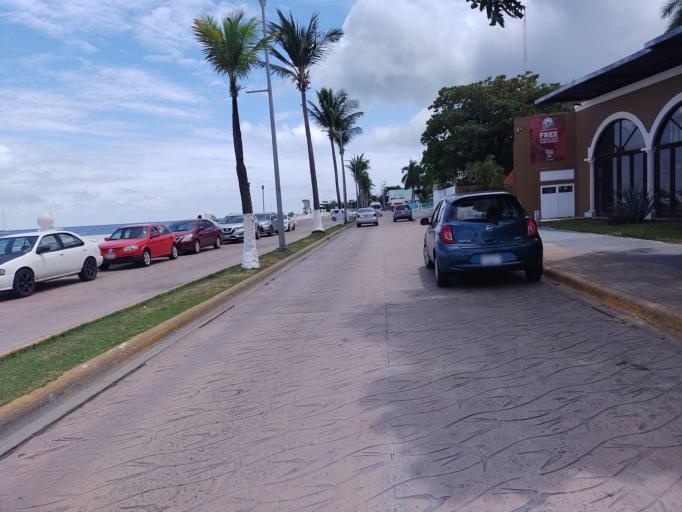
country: MX
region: Quintana Roo
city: San Miguel de Cozumel
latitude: 20.5153
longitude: -86.9464
